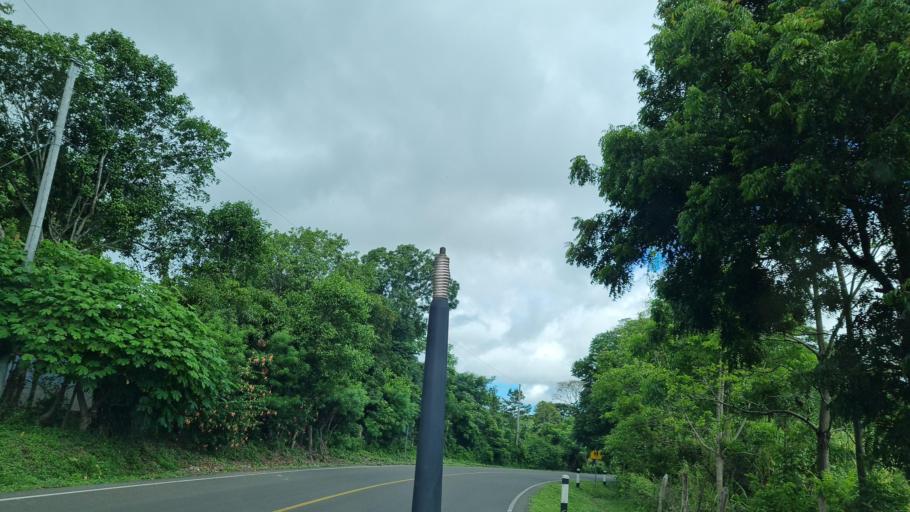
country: NI
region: Boaco
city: San Jose de los Remates
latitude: 12.5953
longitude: -85.8993
